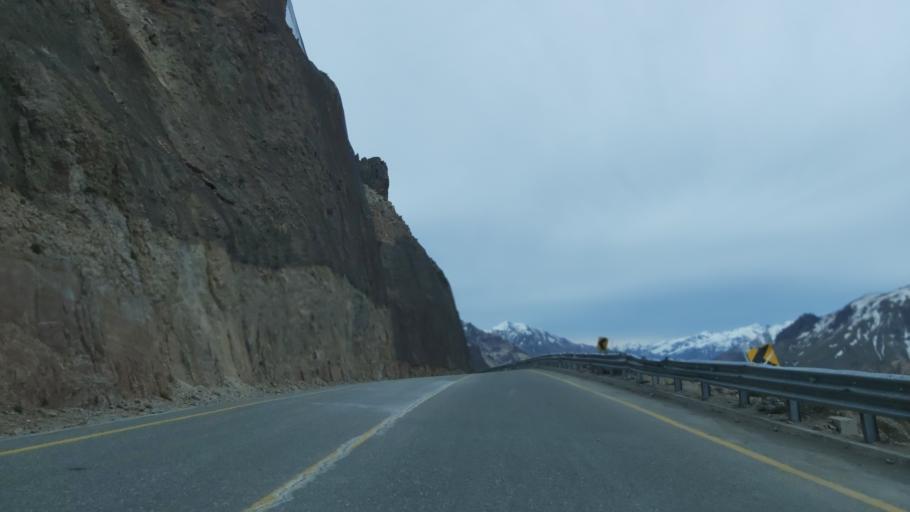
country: CL
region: Maule
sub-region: Provincia de Linares
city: Colbun
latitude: -35.9563
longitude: -70.5785
